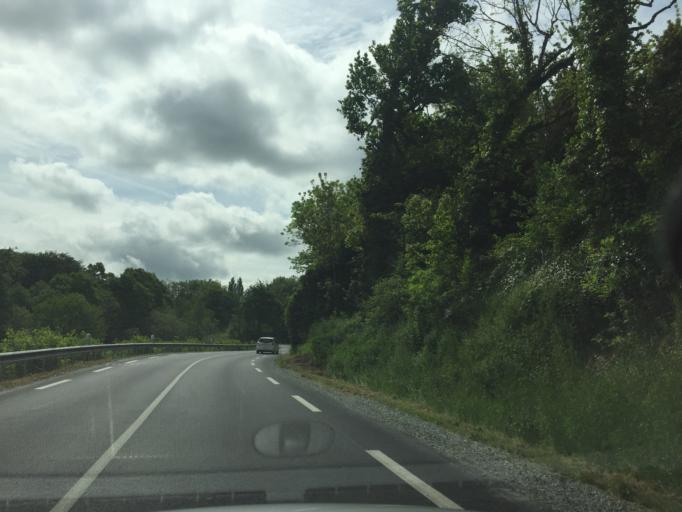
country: FR
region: Brittany
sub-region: Departement des Cotes-d'Armor
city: Crehen
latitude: 48.5702
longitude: -2.2118
